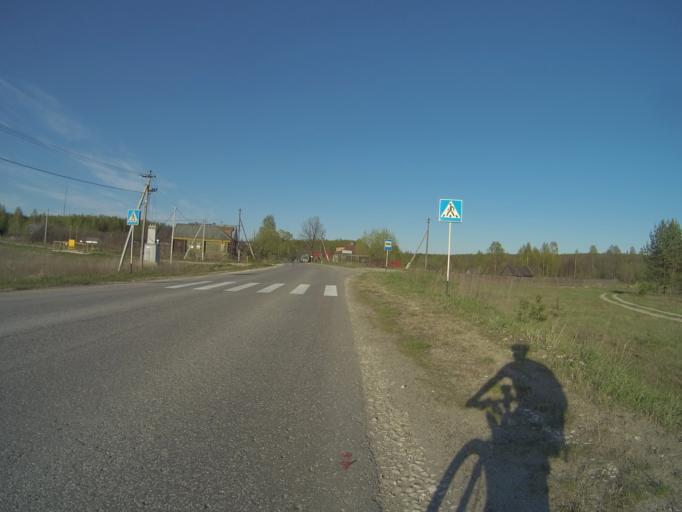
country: RU
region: Vladimir
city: Sudogda
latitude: 56.0791
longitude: 40.7724
